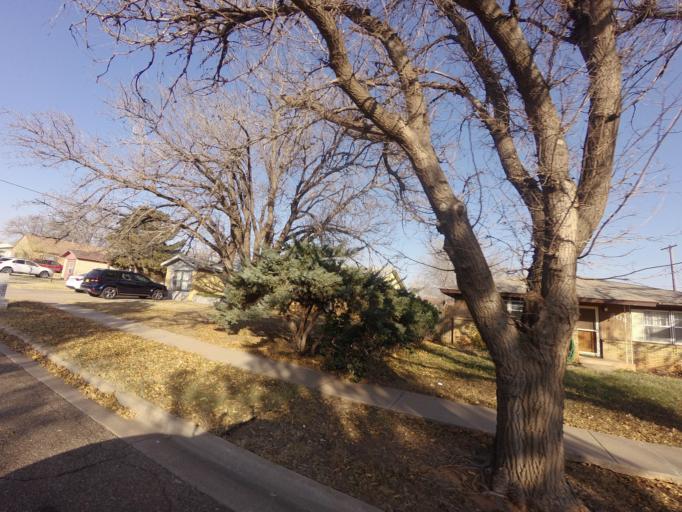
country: US
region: New Mexico
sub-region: Curry County
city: Clovis
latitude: 34.4176
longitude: -103.2118
